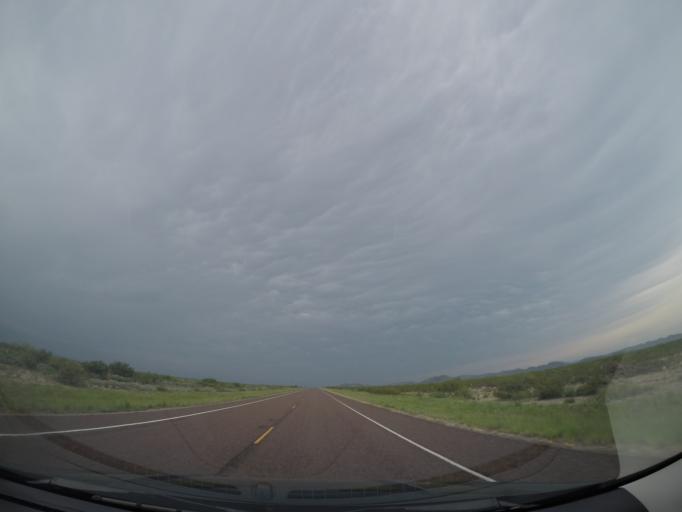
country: US
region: Texas
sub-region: Brewster County
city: Alpine
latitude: 30.0916
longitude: -103.2632
